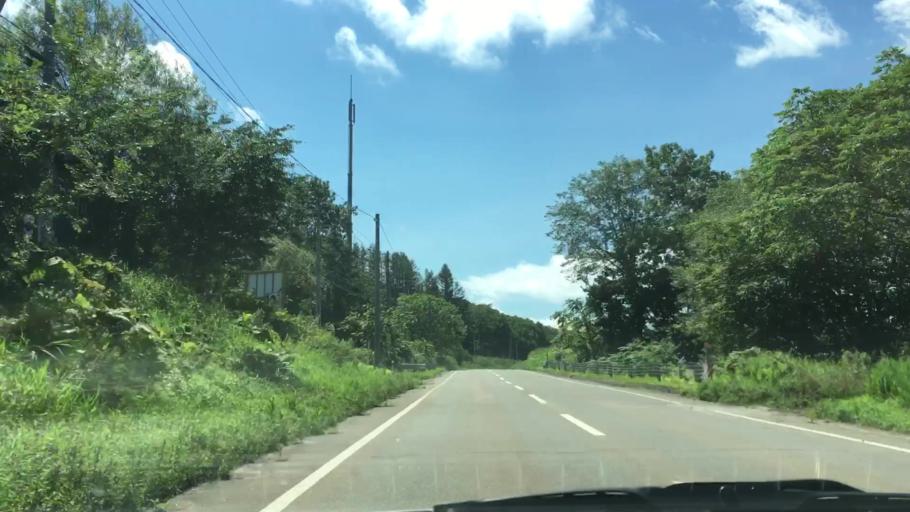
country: JP
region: Hokkaido
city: Kitami
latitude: 43.3253
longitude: 143.7319
